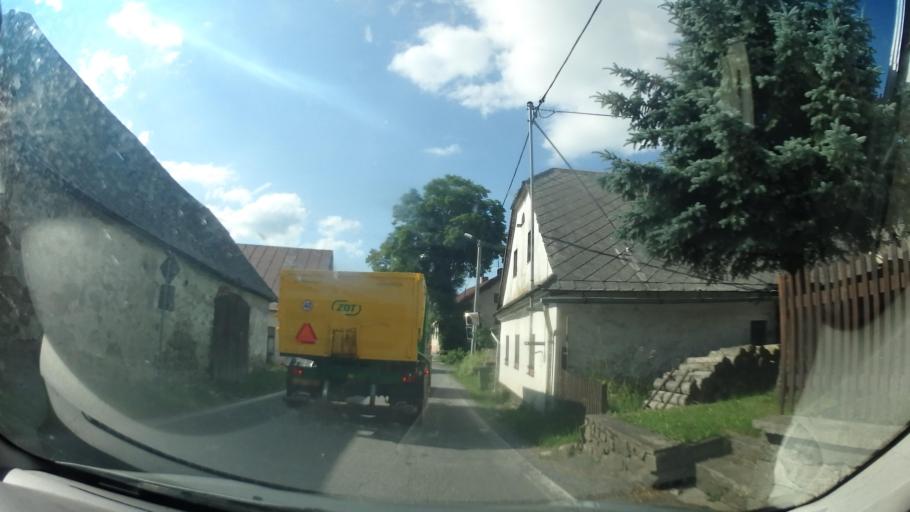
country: CZ
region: Vysocina
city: Heralec
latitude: 49.6889
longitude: 15.9931
